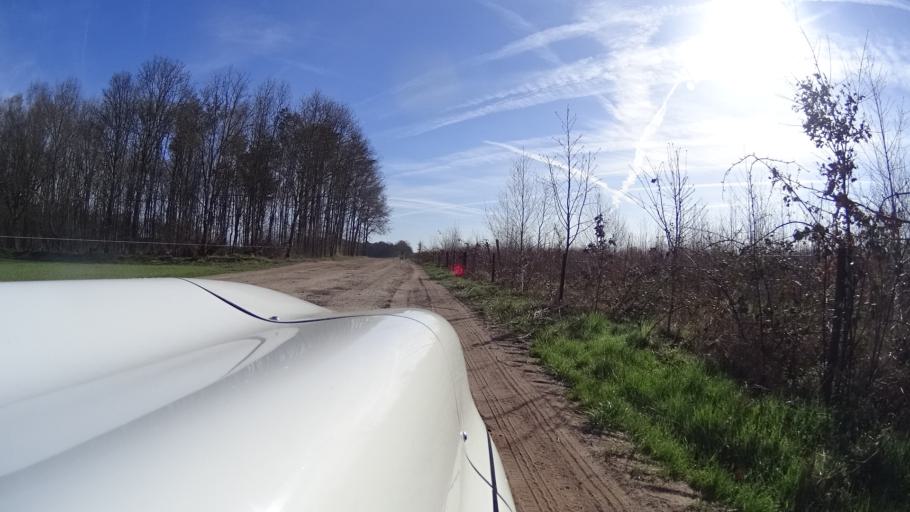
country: NL
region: North Brabant
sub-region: Gemeente Uden
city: Odiliapeel
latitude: 51.6734
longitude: 5.7172
